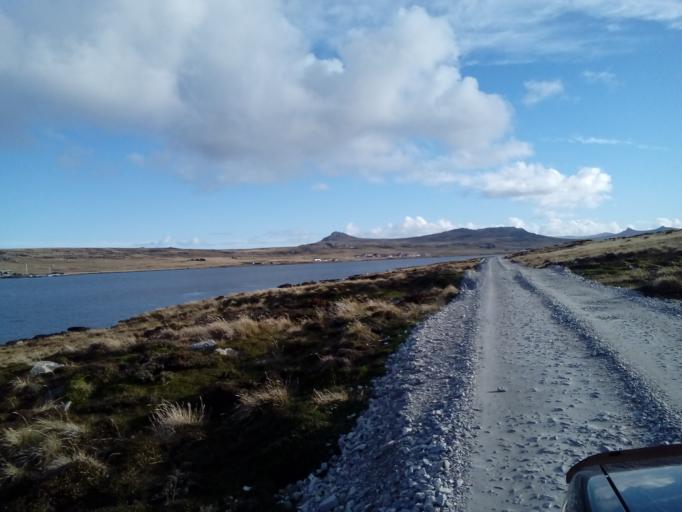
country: FK
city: Stanley
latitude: -51.6831
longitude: -57.8854
